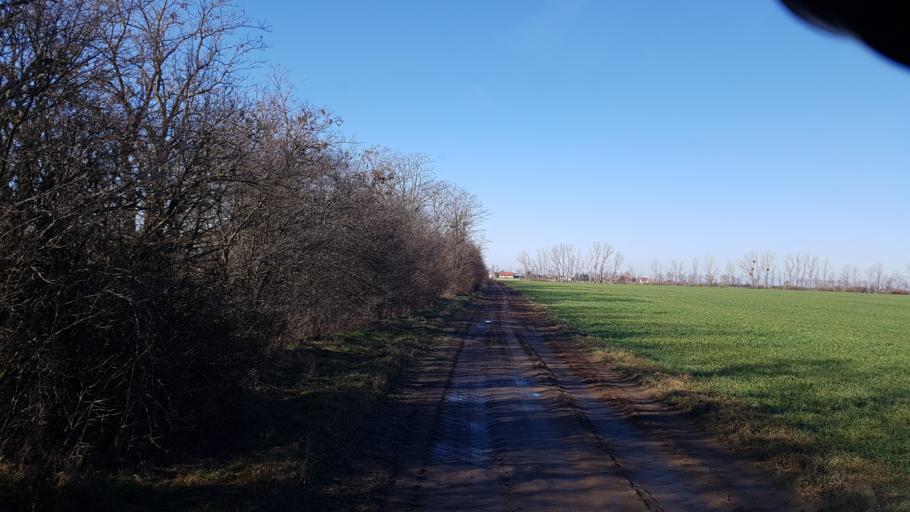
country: DE
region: Brandenburg
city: Muhlberg
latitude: 51.5083
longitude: 13.2428
